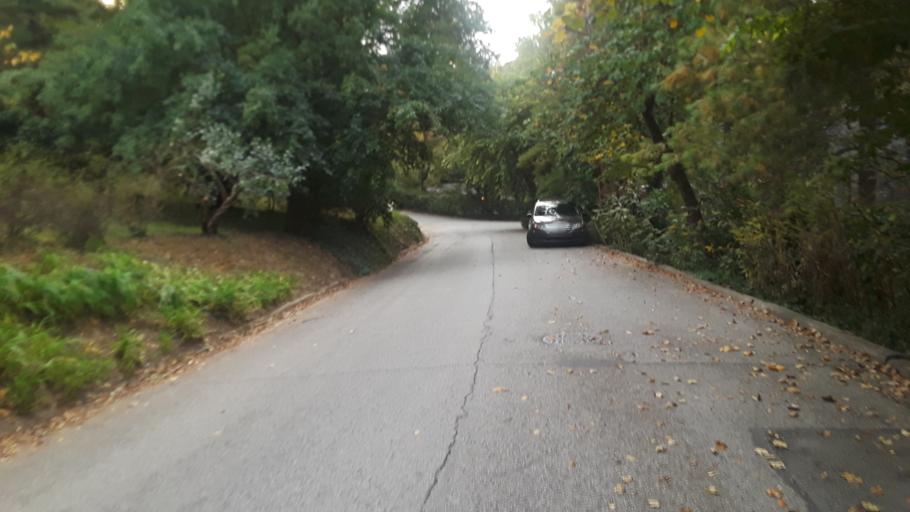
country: US
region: Kentucky
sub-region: Jefferson County
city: Saint Matthews
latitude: 38.2481
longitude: -85.6950
